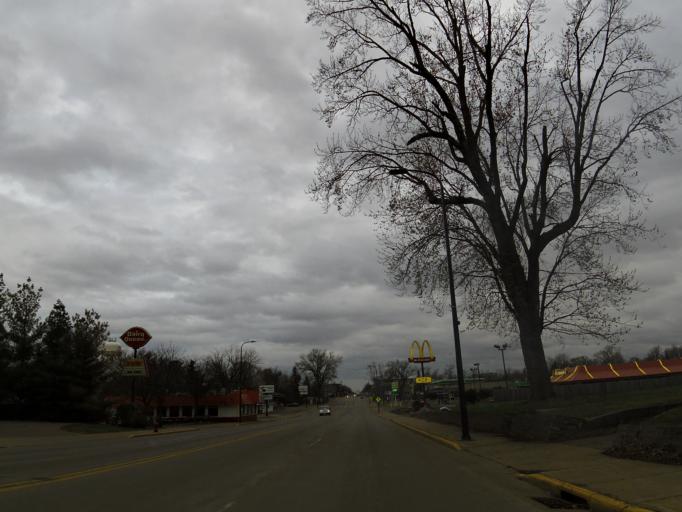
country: US
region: Wisconsin
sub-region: Saint Croix County
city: New Richmond
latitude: 45.1256
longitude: -92.5377
